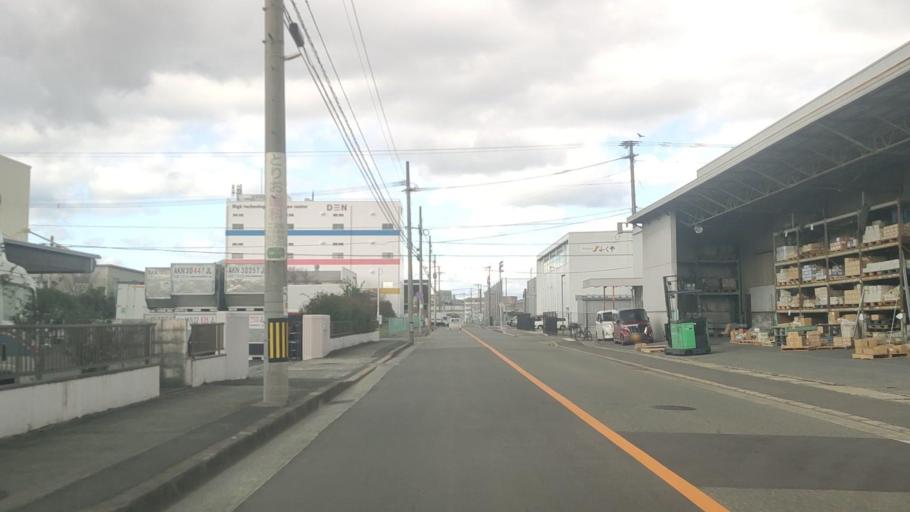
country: JP
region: Fukuoka
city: Fukuoka-shi
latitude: 33.6093
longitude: 130.4352
